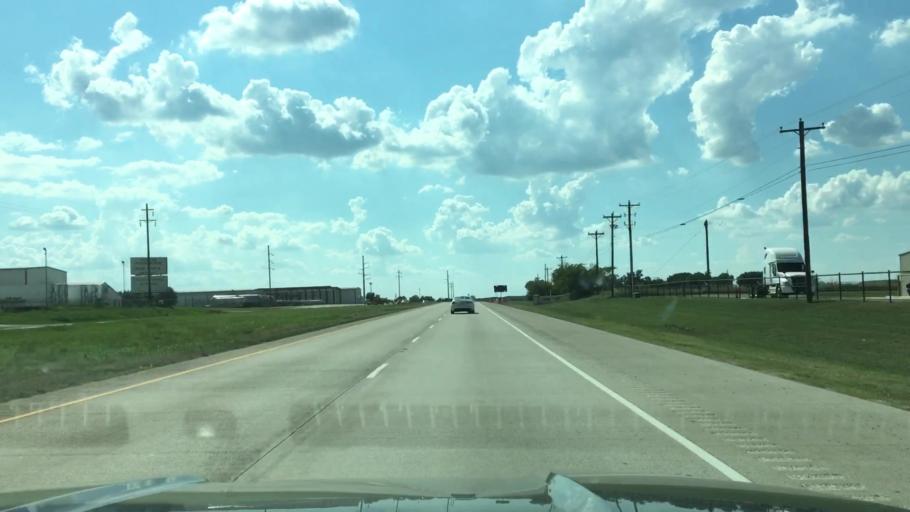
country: US
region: Texas
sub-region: Wise County
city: Rhome
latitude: 33.0370
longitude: -97.4353
